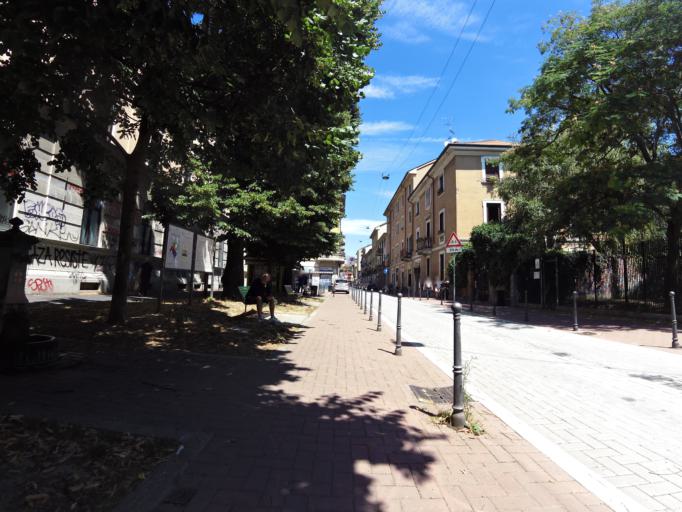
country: IT
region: Lombardy
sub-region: Citta metropolitana di Milano
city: Novegro-Tregarezzo-San Felice
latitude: 45.4821
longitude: 9.2425
